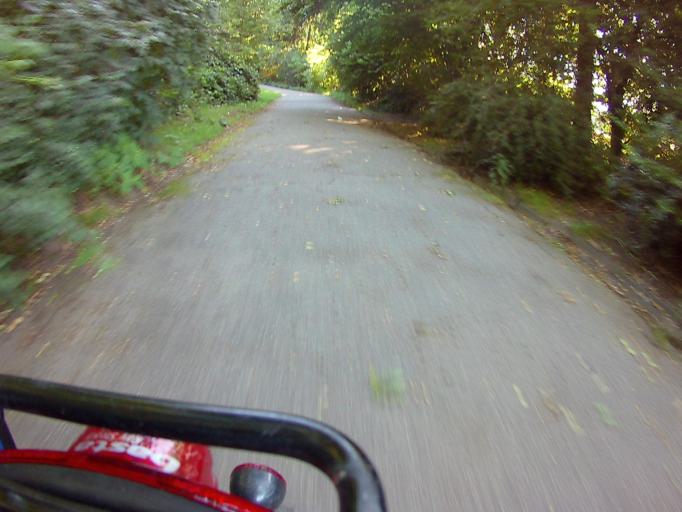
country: DE
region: Hamburg
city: Harburg
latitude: 53.4507
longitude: 9.9796
